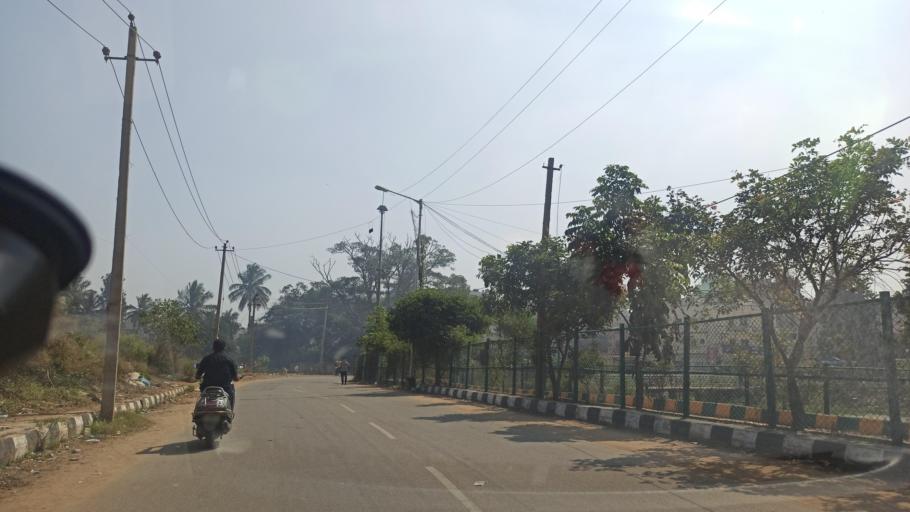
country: IN
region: Karnataka
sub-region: Bangalore Urban
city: Yelahanka
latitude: 13.0607
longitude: 77.5996
